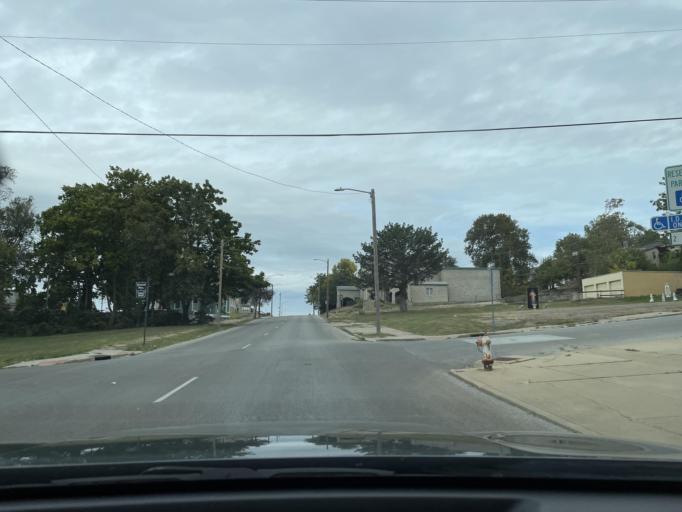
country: US
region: Missouri
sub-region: Buchanan County
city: Saint Joseph
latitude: 39.7633
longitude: -94.8480
